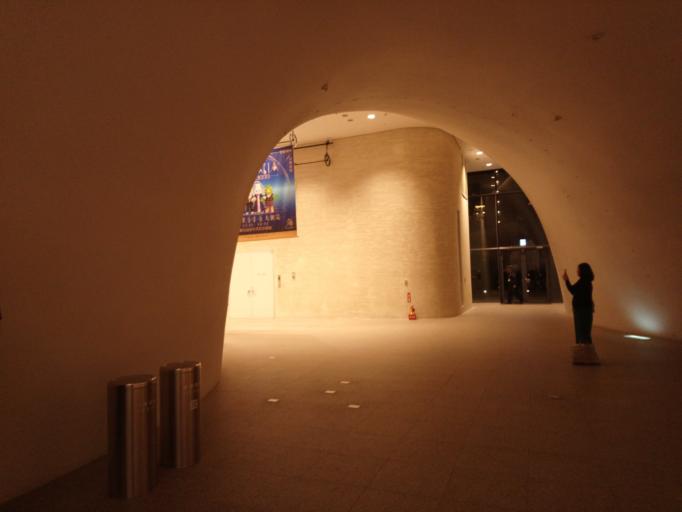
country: TW
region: Taiwan
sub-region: Taichung City
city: Taichung
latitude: 24.1629
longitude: 120.6403
